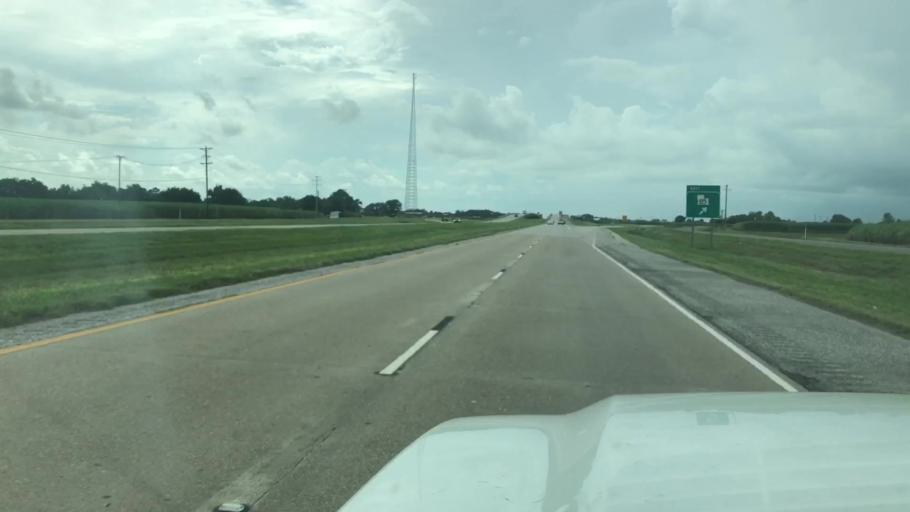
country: US
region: Louisiana
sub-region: Iberia Parish
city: Jeanerette
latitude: 29.9158
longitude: -91.7225
